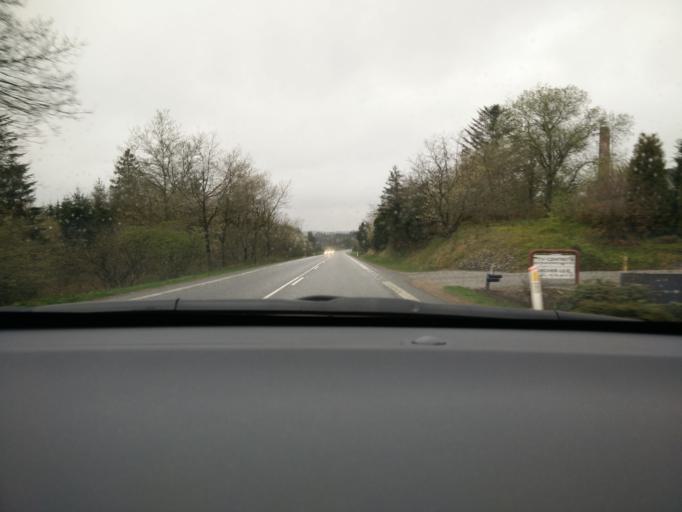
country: DK
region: Central Jutland
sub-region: Viborg Kommune
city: Stoholm
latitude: 56.5139
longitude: 9.2724
